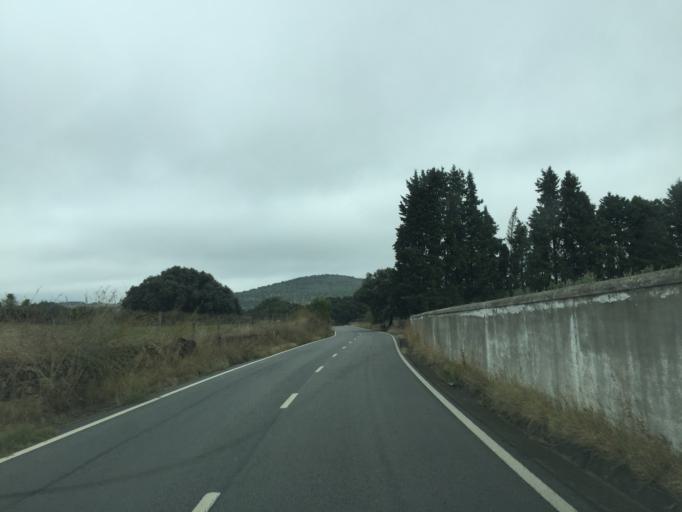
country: PT
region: Portalegre
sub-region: Alter do Chao
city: Alter do Chao
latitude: 39.2170
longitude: -7.6543
